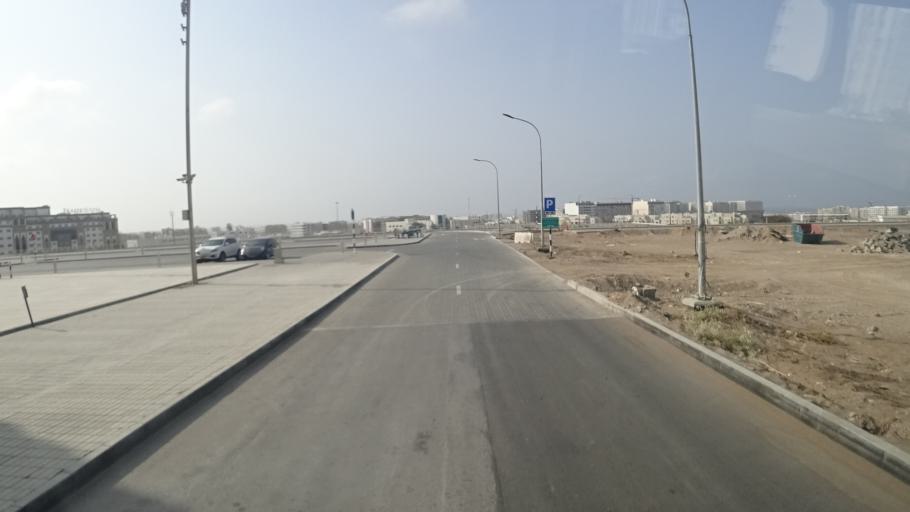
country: OM
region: Muhafazat Masqat
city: Bawshar
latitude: 23.5790
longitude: 58.4152
